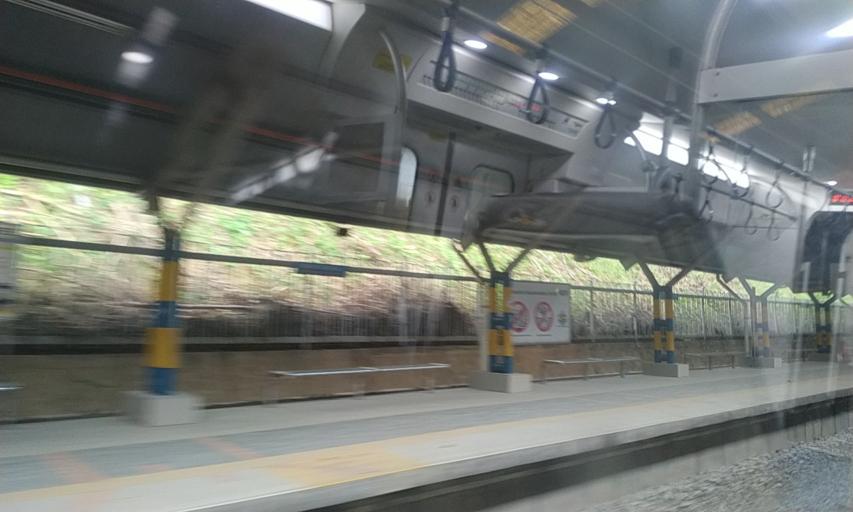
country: MY
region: Kuala Lumpur
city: Kuala Lumpur
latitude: 3.1543
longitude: 101.6929
